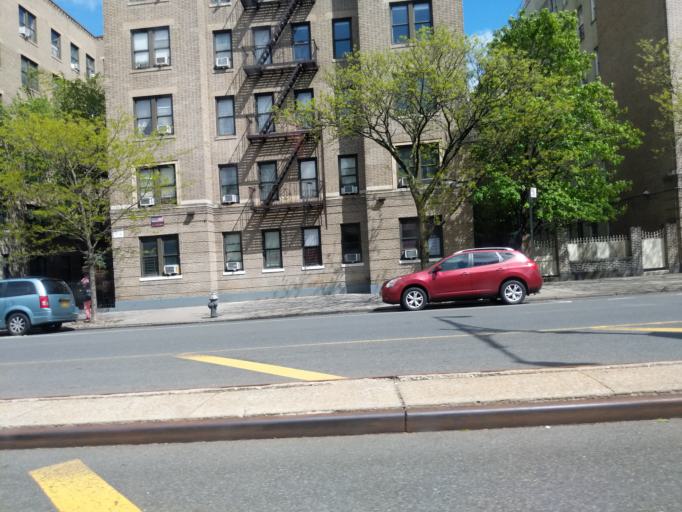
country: US
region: New York
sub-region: New York County
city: Inwood
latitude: 40.8240
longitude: -73.9243
